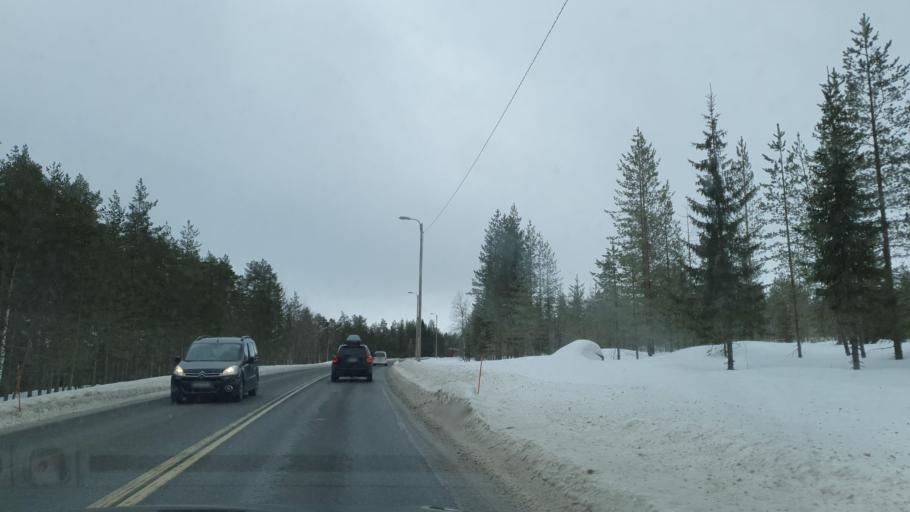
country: FI
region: Lapland
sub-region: Torniolaakso
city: Ylitornio
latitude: 66.2118
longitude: 23.7972
